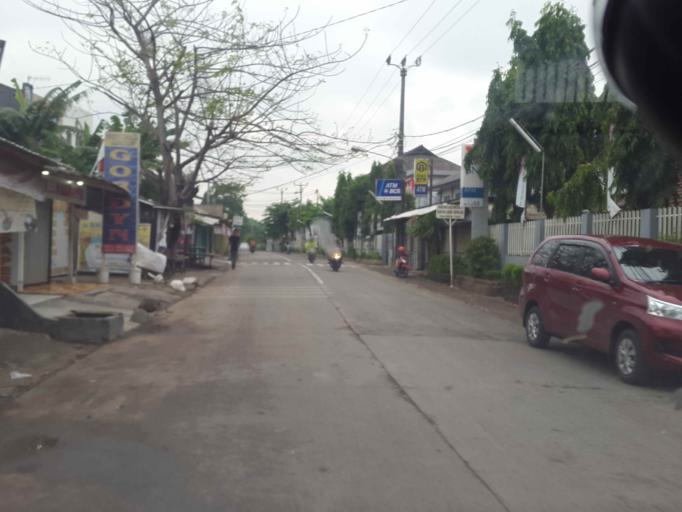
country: ID
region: West Java
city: Bekasi
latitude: -6.2321
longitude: 107.0217
